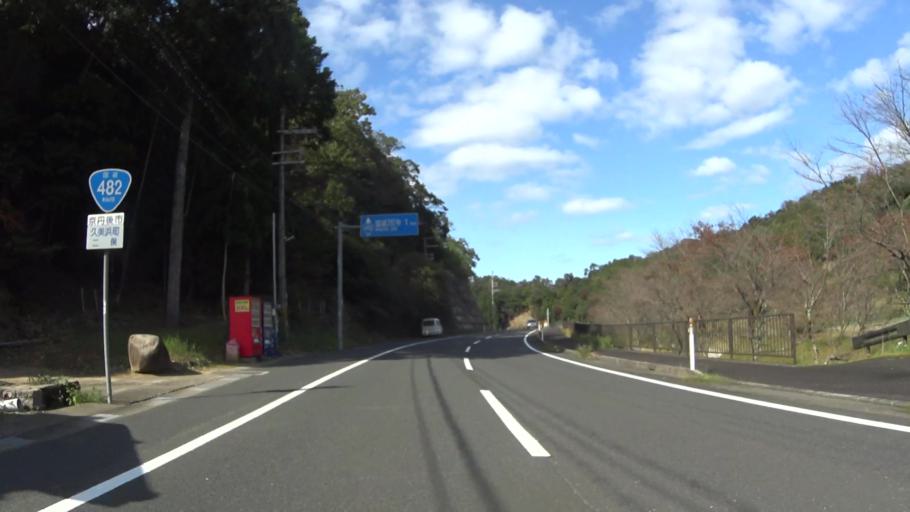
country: JP
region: Hyogo
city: Toyooka
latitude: 35.5620
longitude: 134.9784
